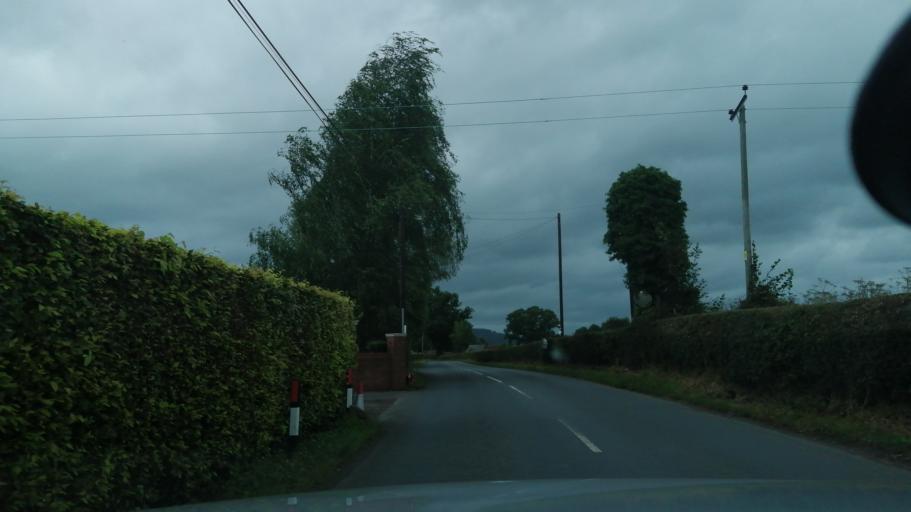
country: GB
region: England
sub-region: Herefordshire
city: Thruxton
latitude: 52.0081
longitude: -2.8132
